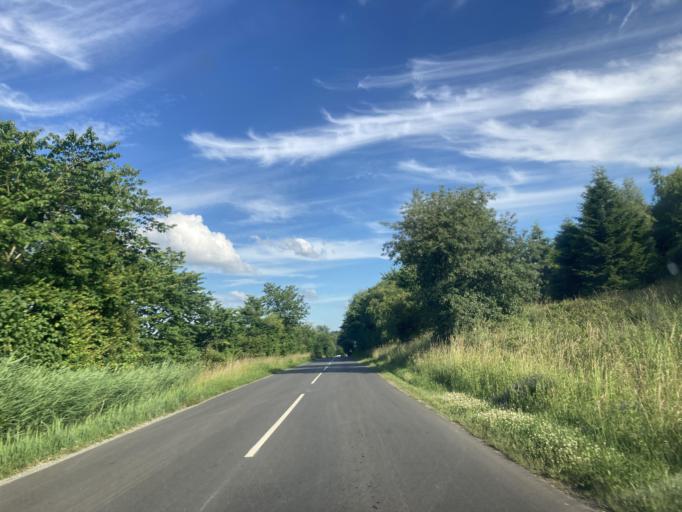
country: DK
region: South Denmark
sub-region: Kolding Kommune
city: Kolding
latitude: 55.4833
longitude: 9.4084
